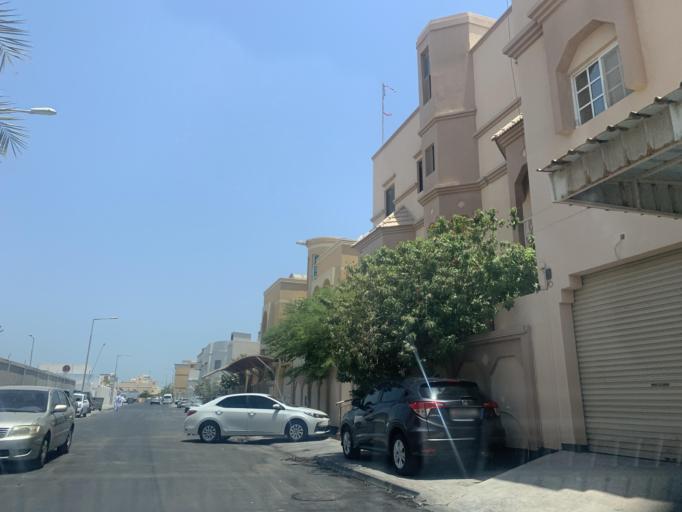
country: BH
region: Muharraq
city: Al Muharraq
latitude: 26.2867
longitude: 50.6240
